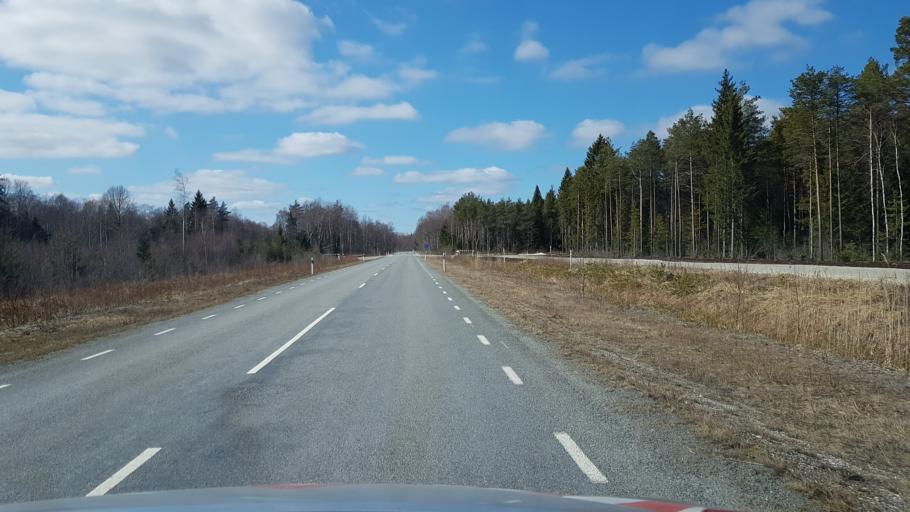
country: EE
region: Laeaene-Virumaa
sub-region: Tapa vald
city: Tapa
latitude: 59.2771
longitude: 25.8984
